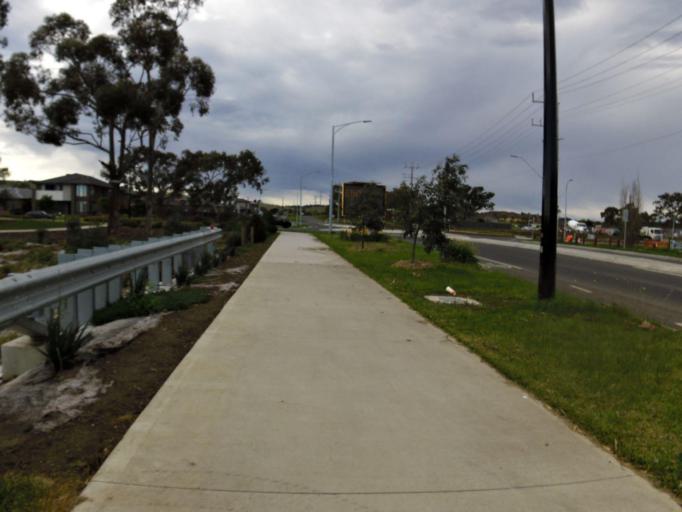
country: AU
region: Victoria
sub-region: Whittlesea
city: Epping
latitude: -37.6240
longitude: 145.0386
